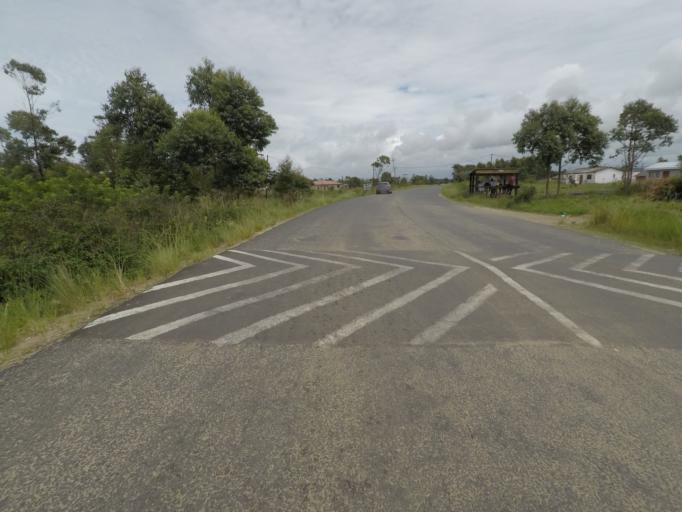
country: ZA
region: KwaZulu-Natal
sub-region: uThungulu District Municipality
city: eSikhawini
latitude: -28.9100
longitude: 31.8781
